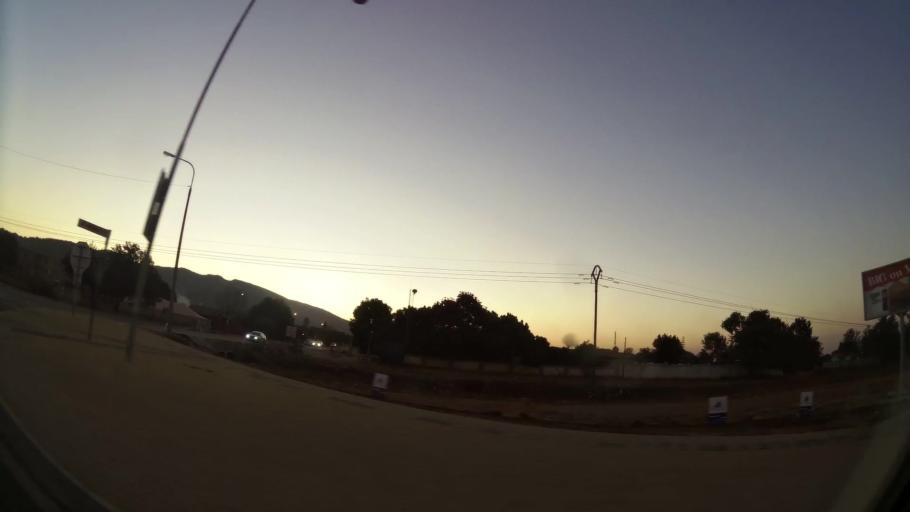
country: ZA
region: North-West
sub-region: Bojanala Platinum District Municipality
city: Rustenburg
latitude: -25.6591
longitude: 27.2149
